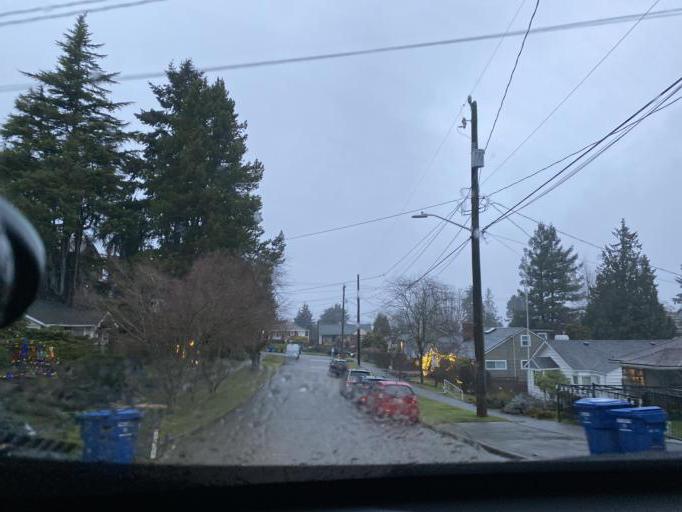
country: US
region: Washington
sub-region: King County
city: Seattle
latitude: 47.6568
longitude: -122.3969
